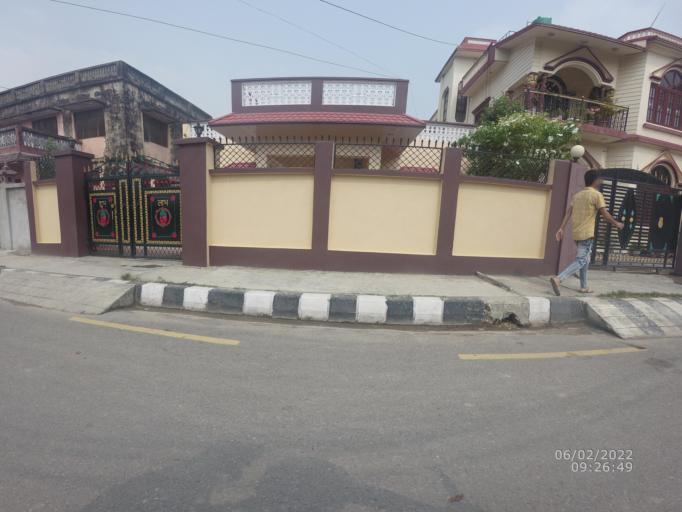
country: NP
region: Western Region
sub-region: Lumbini Zone
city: Bhairahawa
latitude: 27.4993
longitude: 83.4515
